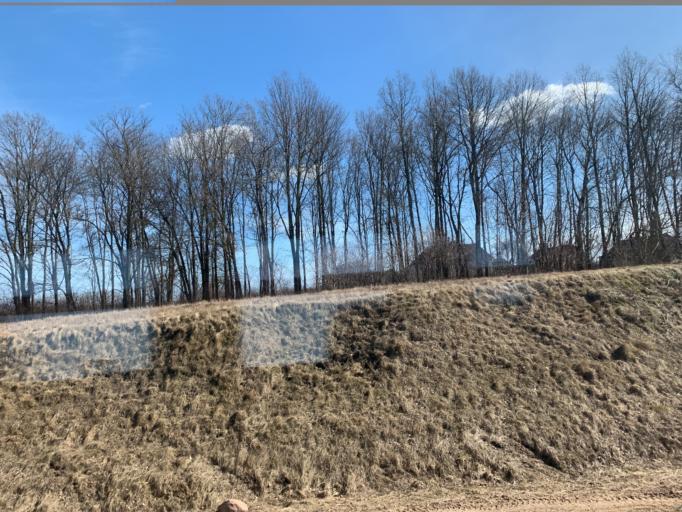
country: BY
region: Minsk
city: Haradzyeya
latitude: 53.3257
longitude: 26.5434
